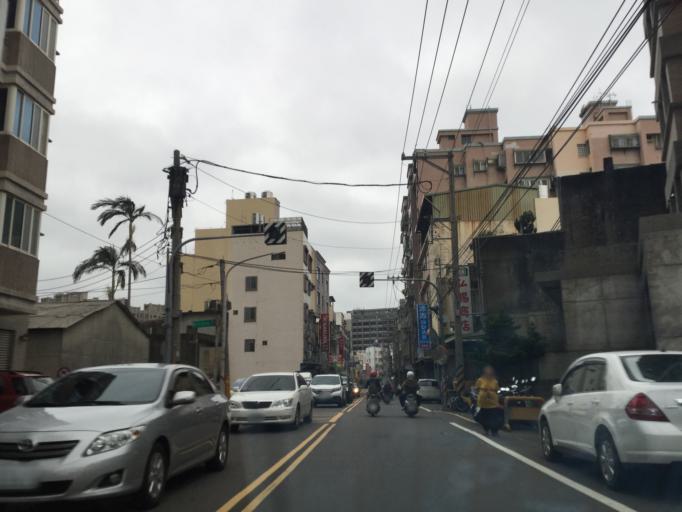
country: TW
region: Taiwan
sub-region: Hsinchu
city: Zhubei
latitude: 24.7942
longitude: 121.0124
